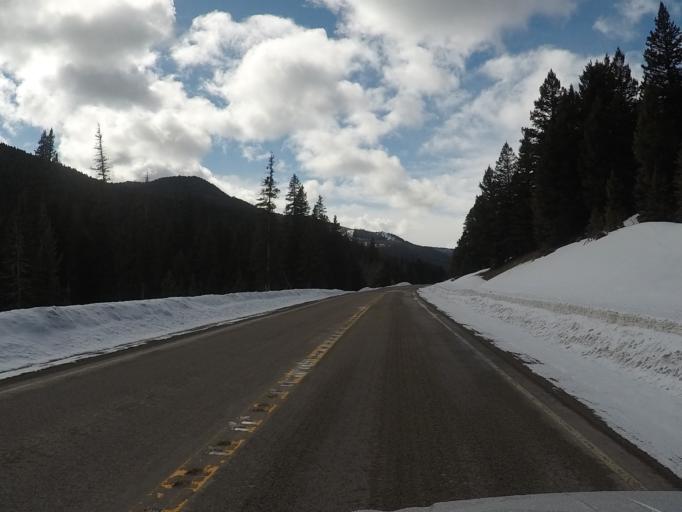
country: US
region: Montana
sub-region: Meagher County
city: White Sulphur Springs
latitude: 46.7602
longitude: -110.7298
